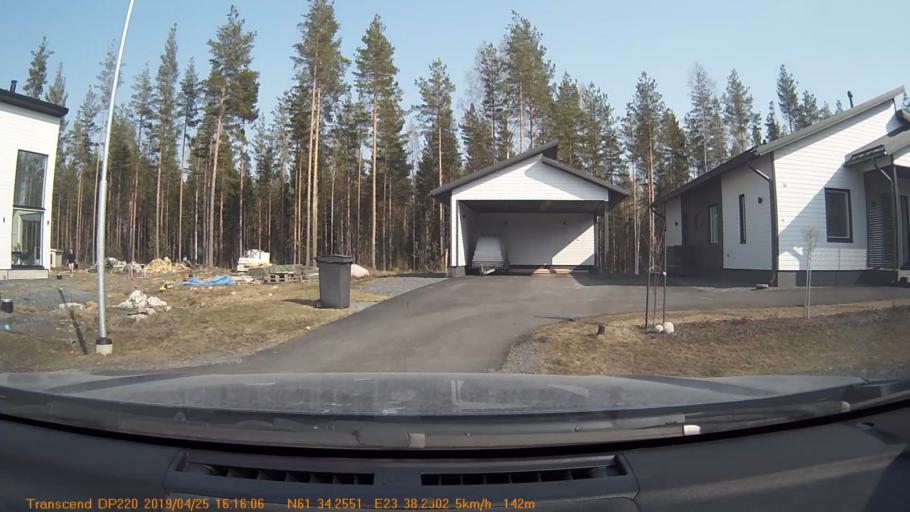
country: FI
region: Pirkanmaa
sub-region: Tampere
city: Yloejaervi
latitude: 61.5709
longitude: 23.6370
